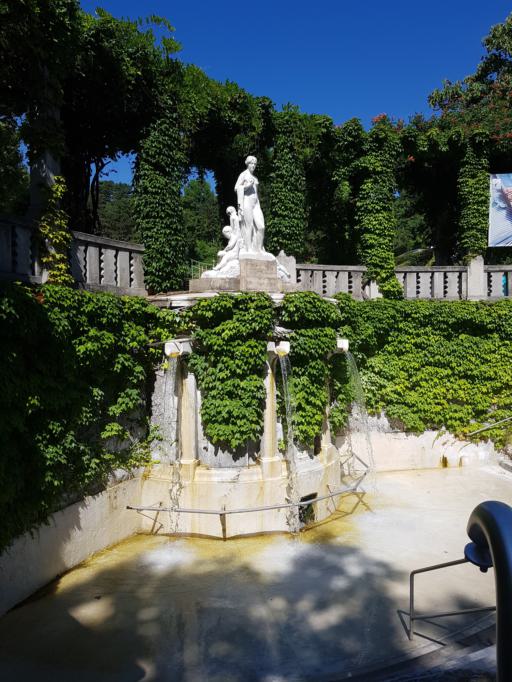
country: AT
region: Lower Austria
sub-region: Politischer Bezirk Baden
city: Bad Voslau
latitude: 47.9672
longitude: 16.2118
